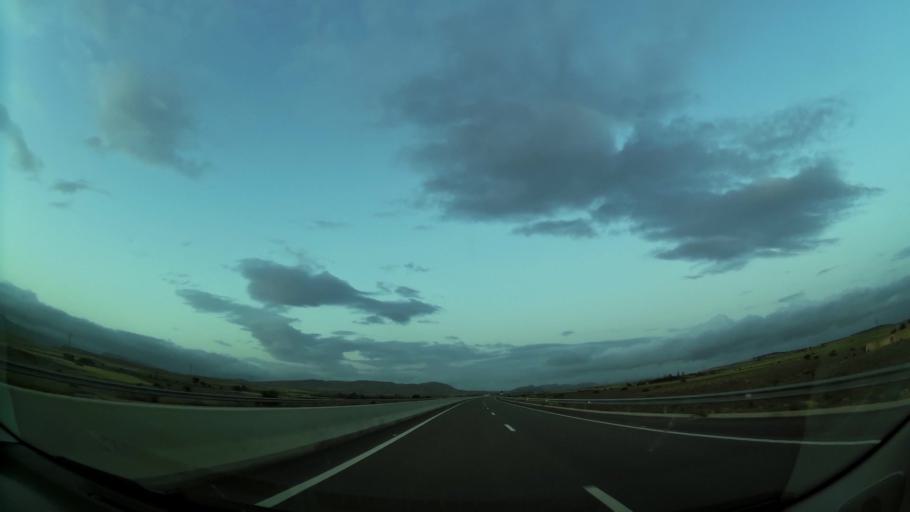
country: MA
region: Oriental
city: El Aioun
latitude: 34.6257
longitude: -2.5325
